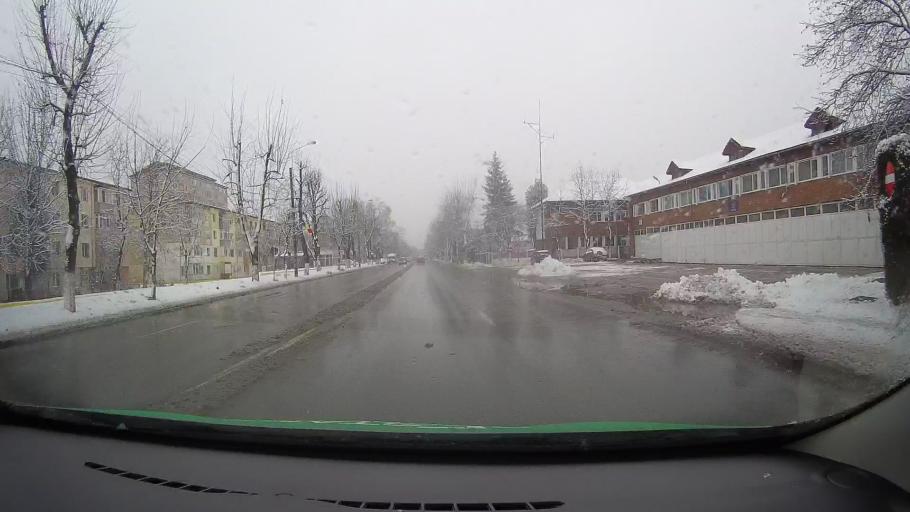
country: RO
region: Hunedoara
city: Hunedoara
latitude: 45.7600
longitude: 22.9018
